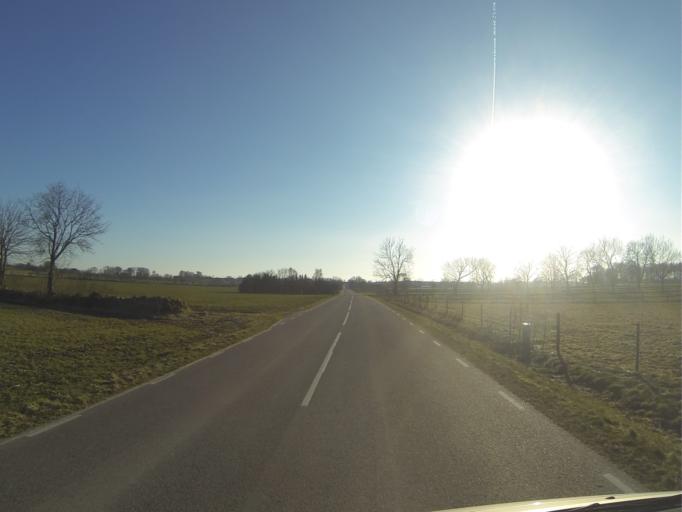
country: SE
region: Skane
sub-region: Hoors Kommun
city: Loberod
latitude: 55.7847
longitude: 13.5283
